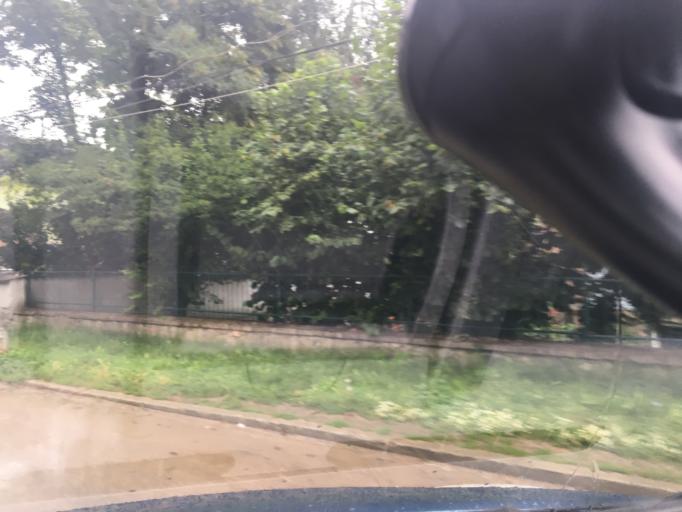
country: BG
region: Sofia-Capital
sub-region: Stolichna Obshtina
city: Sofia
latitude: 42.5849
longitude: 23.3546
